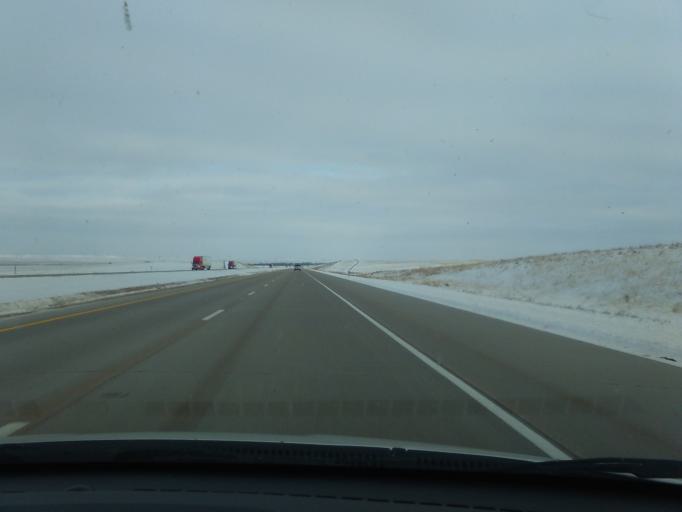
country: US
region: Nebraska
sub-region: Deuel County
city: Chappell
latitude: 41.1132
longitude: -102.5927
